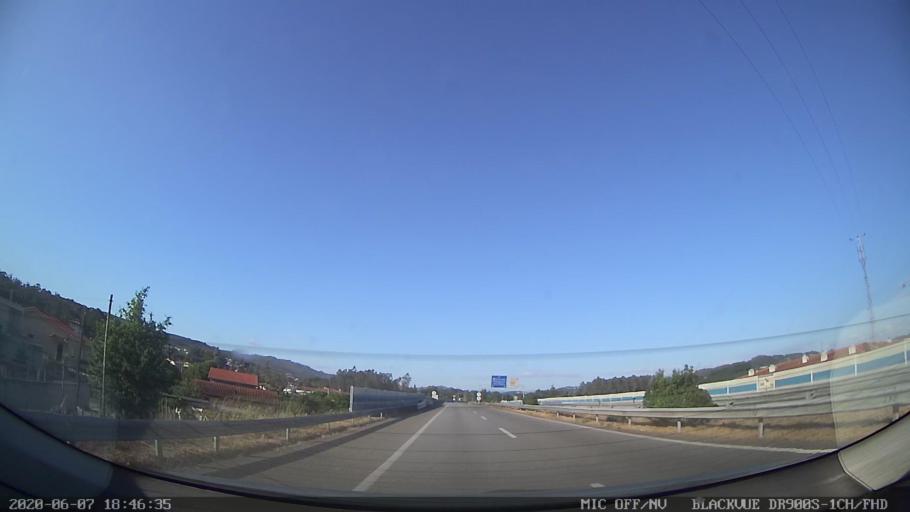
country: PT
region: Braga
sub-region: Vila Nova de Famalicao
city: Vila Nova de Famalicao
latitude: 41.3992
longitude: -8.4668
